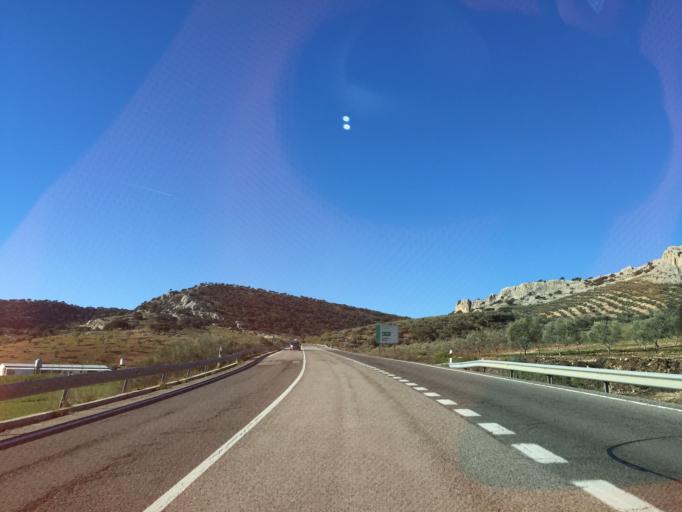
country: ES
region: Andalusia
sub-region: Provincia de Malaga
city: Cuevas del Becerro
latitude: 36.8626
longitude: -5.0591
